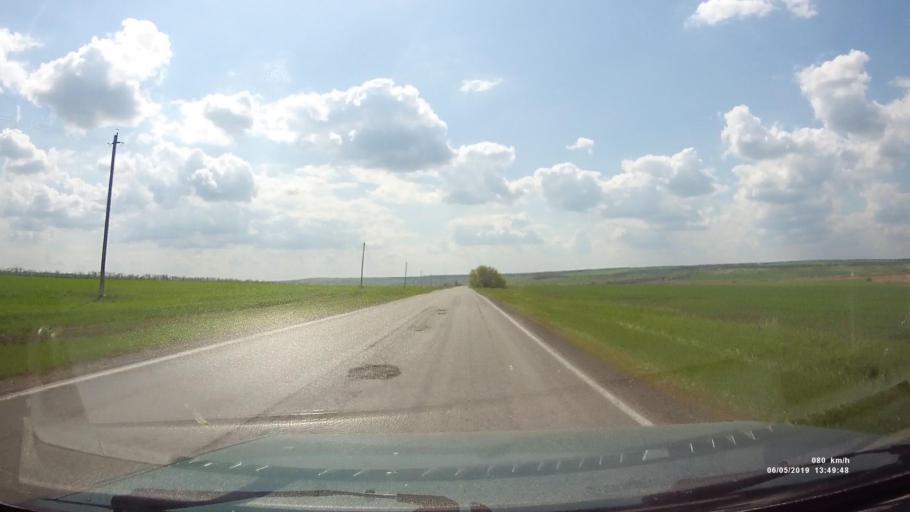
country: RU
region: Rostov
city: Melikhovskaya
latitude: 47.6581
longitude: 40.5192
